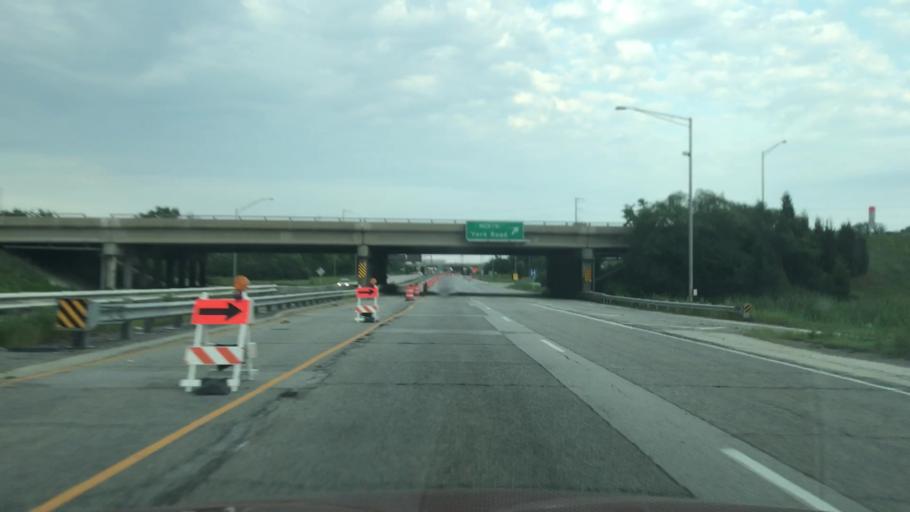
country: US
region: Illinois
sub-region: DuPage County
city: Oak Brook
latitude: 41.8615
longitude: -87.9319
